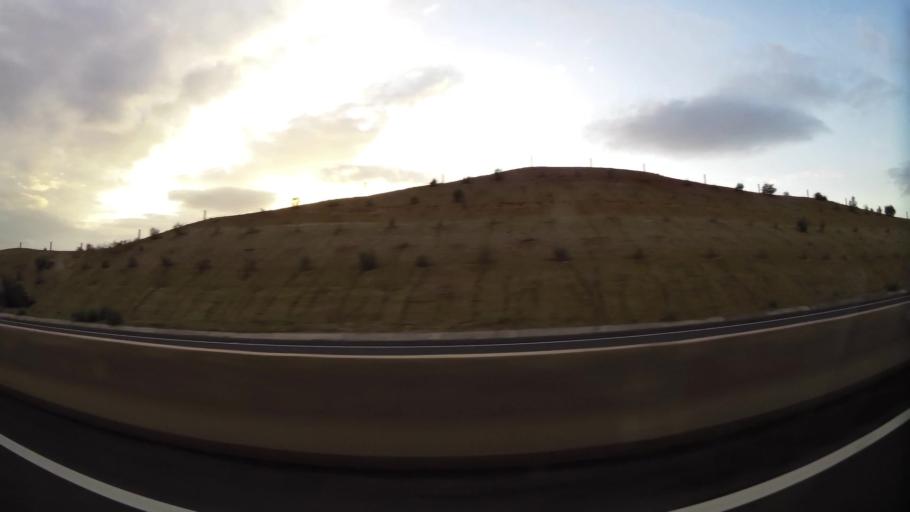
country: MA
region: Oriental
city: Taourirt
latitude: 34.4960
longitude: -2.9676
